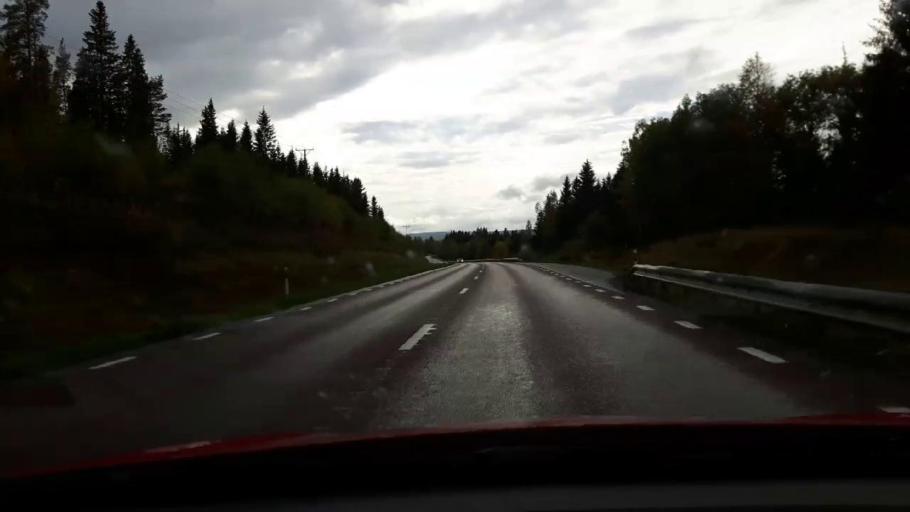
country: SE
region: Jaemtland
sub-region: Bergs Kommun
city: Hoverberg
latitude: 62.7777
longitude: 14.4491
